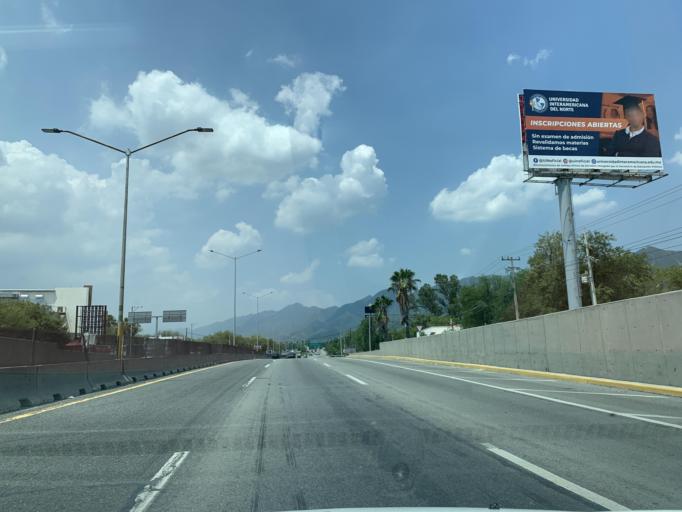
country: MX
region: Nuevo Leon
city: Santiago
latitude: 25.4335
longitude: -100.1526
